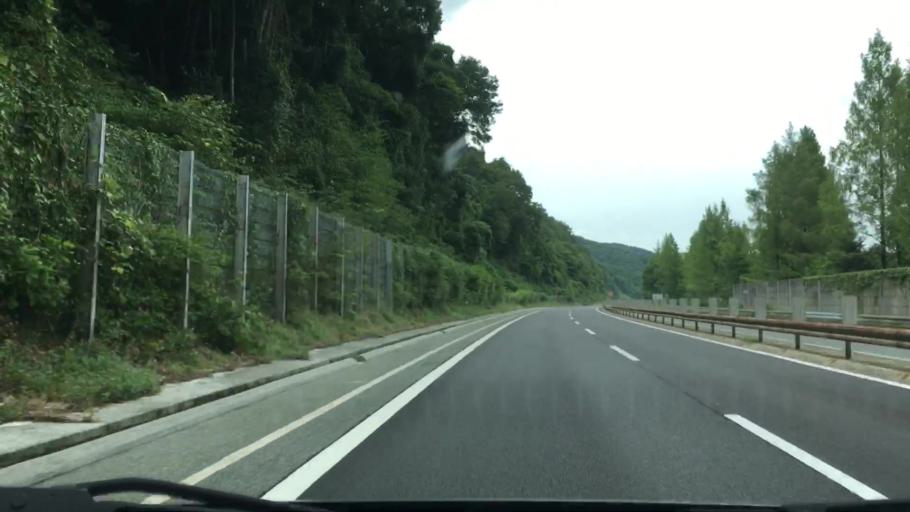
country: JP
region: Okayama
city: Niimi
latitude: 34.9734
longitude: 133.6223
